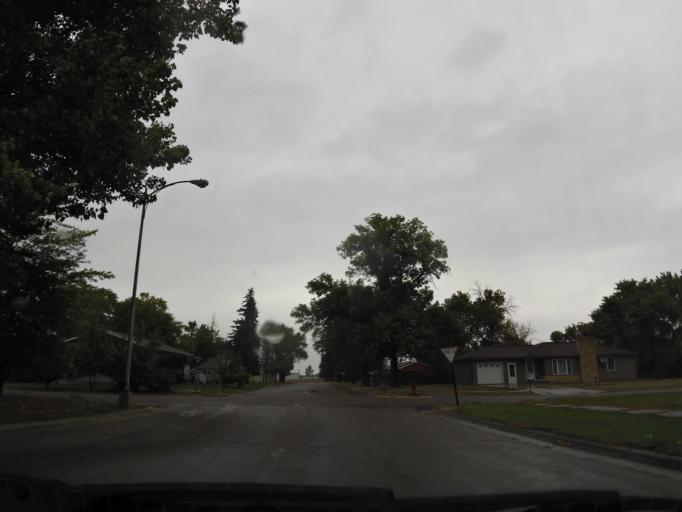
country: US
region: Minnesota
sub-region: Marshall County
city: Warren
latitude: 48.4514
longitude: -96.8713
